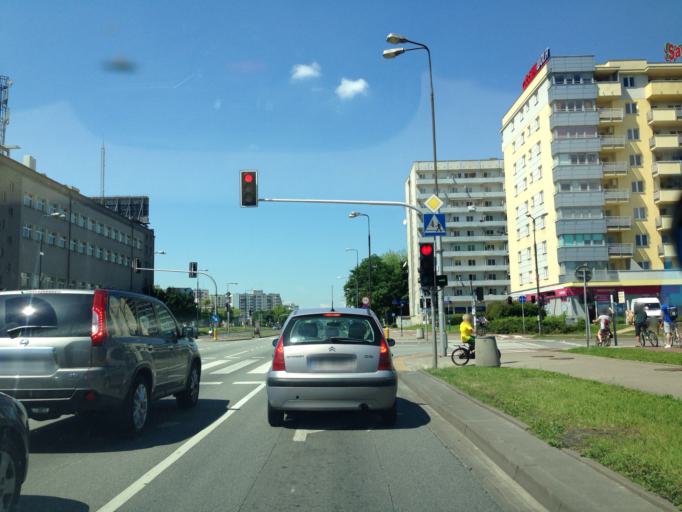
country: PL
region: Masovian Voivodeship
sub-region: Warszawa
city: Wola
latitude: 52.2387
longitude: 20.9491
